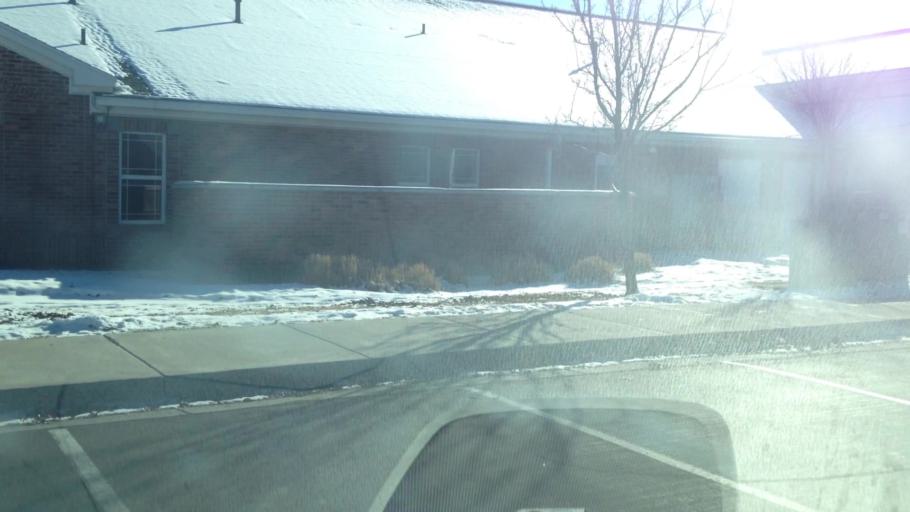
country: US
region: Utah
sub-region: Utah County
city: Orem
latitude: 40.2528
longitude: -111.7108
